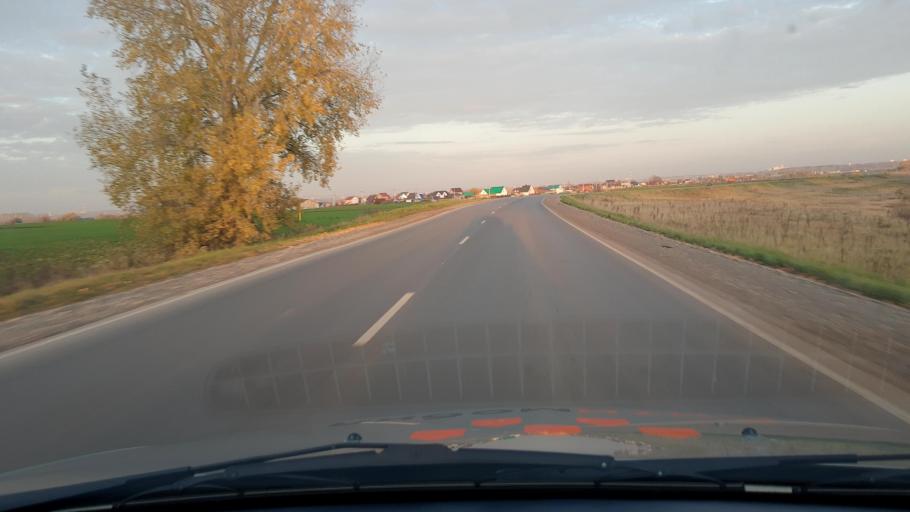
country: RU
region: Bashkortostan
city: Mikhaylovka
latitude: 54.8333
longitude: 55.9348
